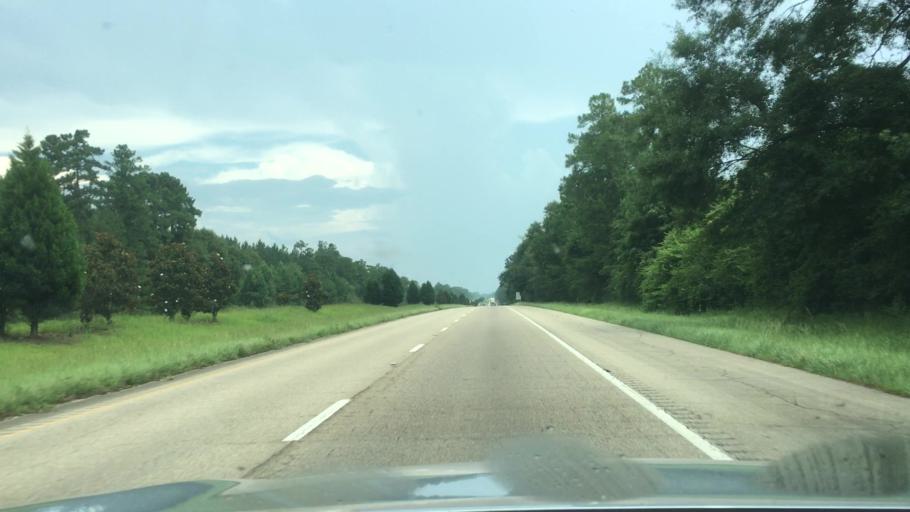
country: US
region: Mississippi
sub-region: Lamar County
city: Lumberton
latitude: 31.0060
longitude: -89.4159
